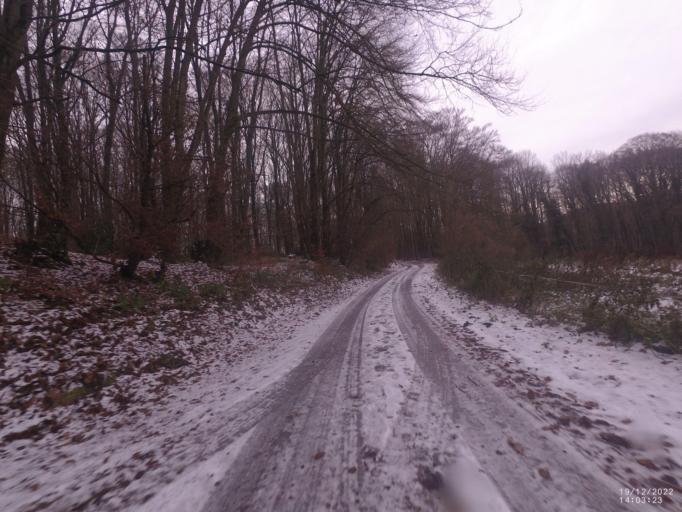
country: DE
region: Rheinland-Pfalz
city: Unkel
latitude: 50.6085
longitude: 7.1815
